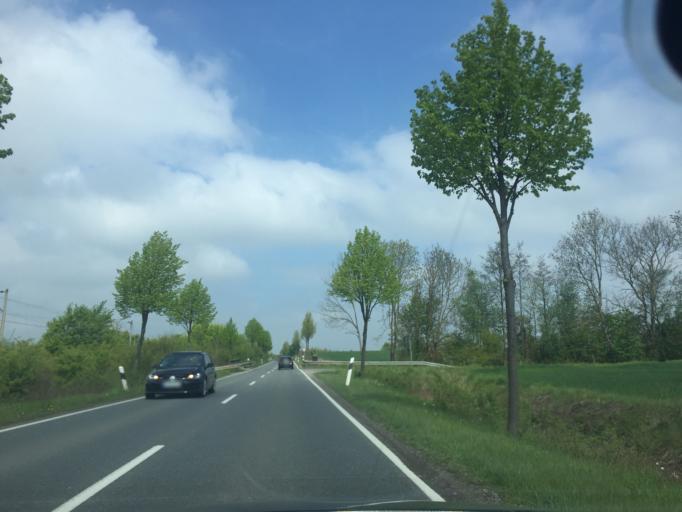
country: DE
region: Lower Saxony
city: Heyersum
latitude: 52.1768
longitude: 9.8393
